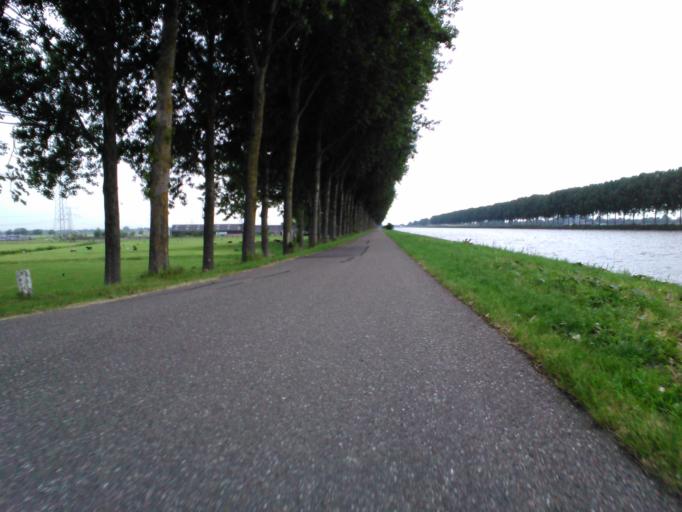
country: NL
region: Utrecht
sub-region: Stichtse Vecht
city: Vreeland
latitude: 52.2592
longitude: 5.0148
